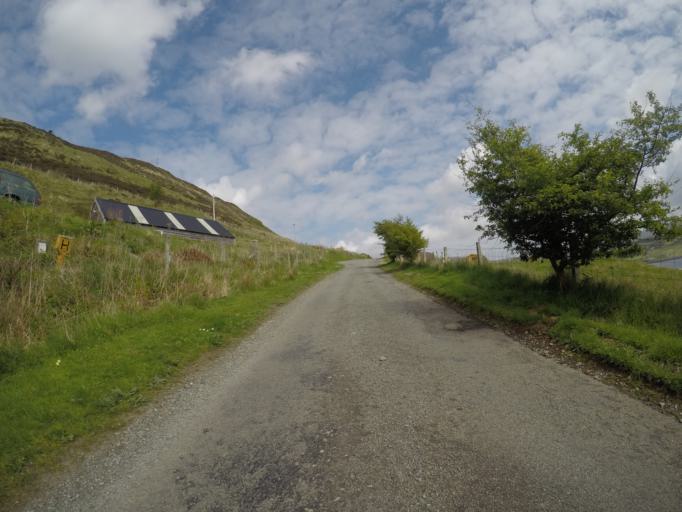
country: GB
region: Scotland
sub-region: Highland
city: Portree
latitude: 57.5884
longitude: -6.3831
